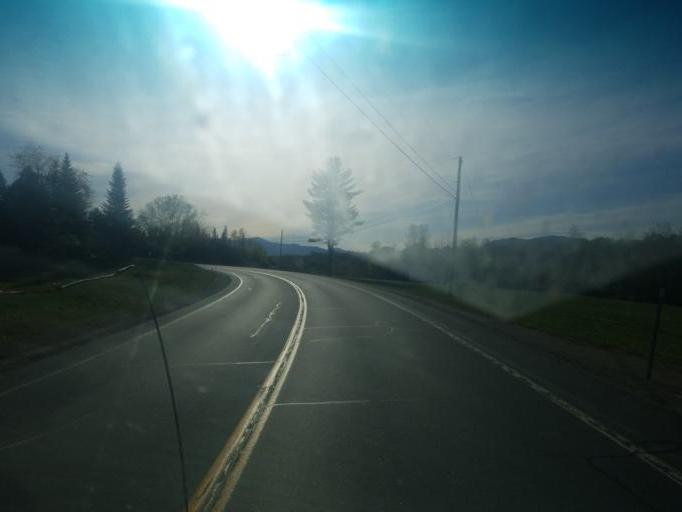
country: US
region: New Hampshire
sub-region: Grafton County
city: Deerfield
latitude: 44.2667
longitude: -71.6191
